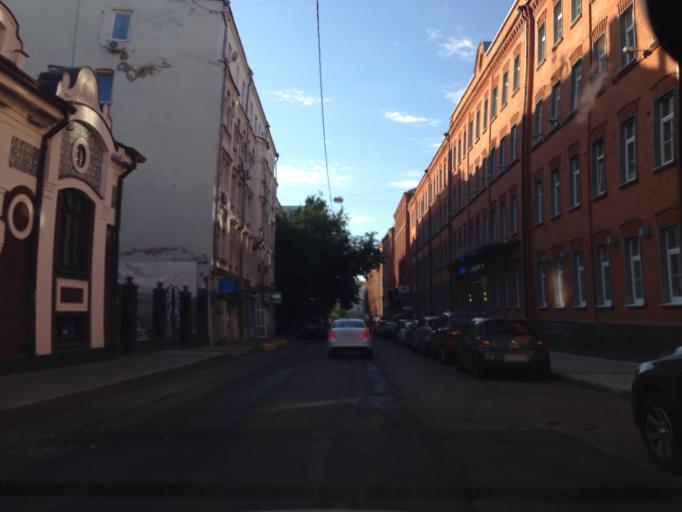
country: RU
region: Moskovskaya
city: Dorogomilovo
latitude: 55.7350
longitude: 37.5882
